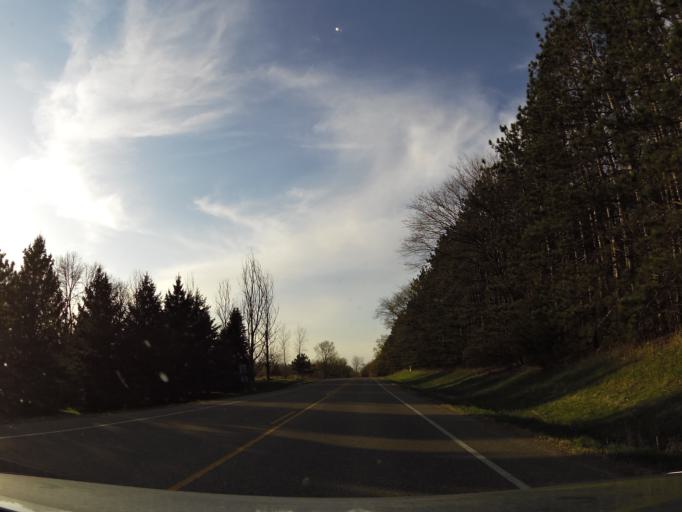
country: US
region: Wisconsin
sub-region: Pierce County
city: River Falls
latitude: 44.9166
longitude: -92.6846
